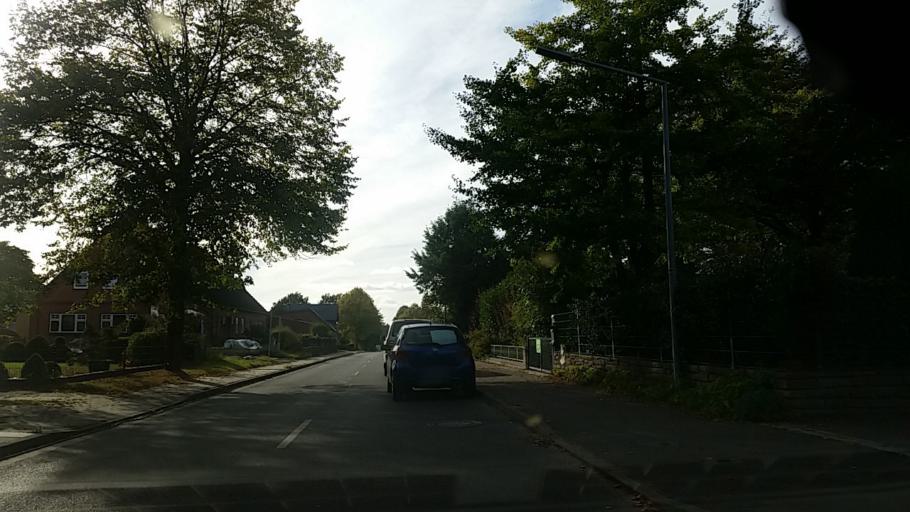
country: DE
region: Schleswig-Holstein
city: Jersbek
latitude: 53.7370
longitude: 10.1938
